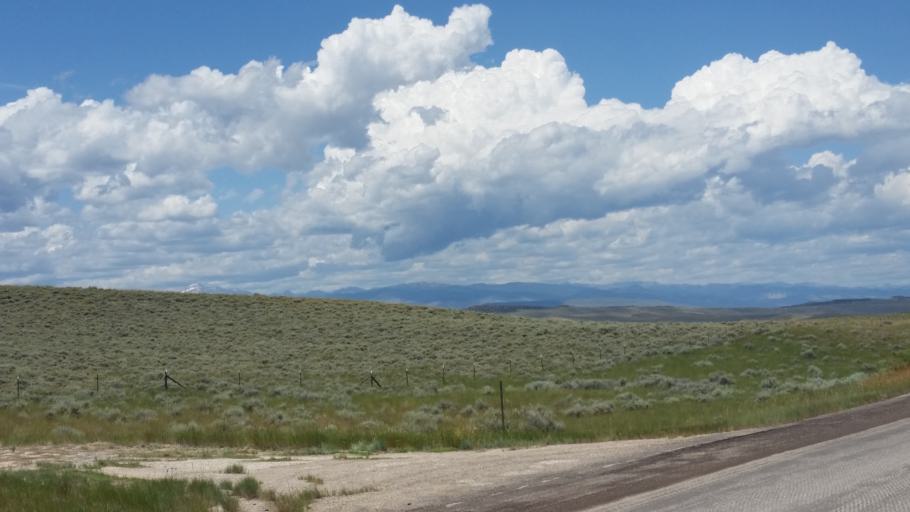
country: US
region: Wyoming
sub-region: Fremont County
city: Arapahoe
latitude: 42.6944
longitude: -108.4575
